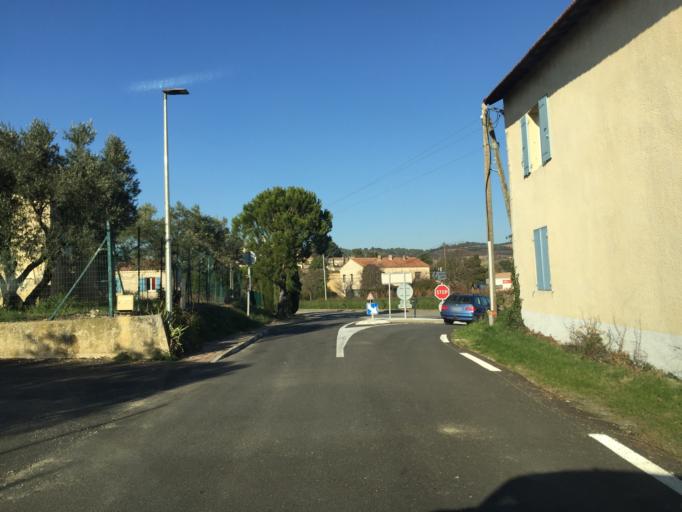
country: FR
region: Provence-Alpes-Cote d'Azur
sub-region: Departement du Vaucluse
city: Sainte-Cecile-les-Vignes
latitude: 44.2272
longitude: 4.9326
